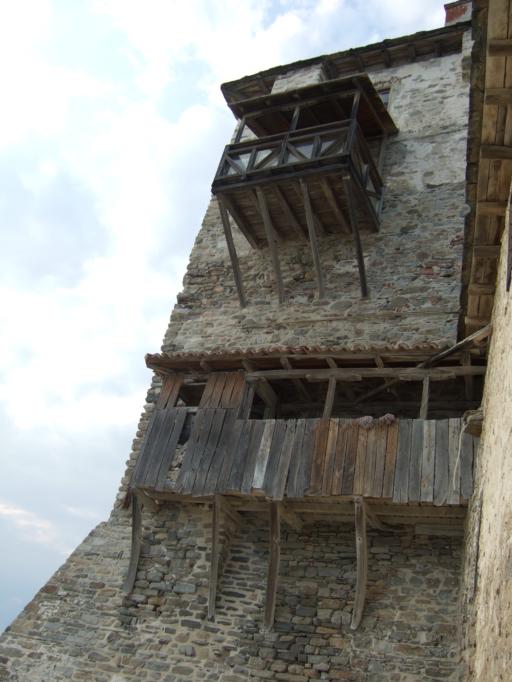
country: GR
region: Central Macedonia
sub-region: Nomos Chalkidikis
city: Ouranoupolis
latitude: 40.3249
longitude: 23.9799
